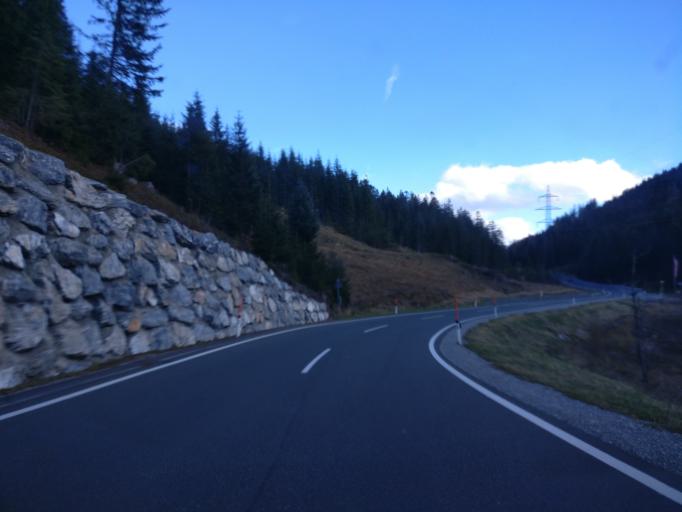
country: AT
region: Salzburg
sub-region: Politischer Bezirk Zell am See
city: Dienten am Hochkonig
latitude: 47.4000
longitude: 12.9947
